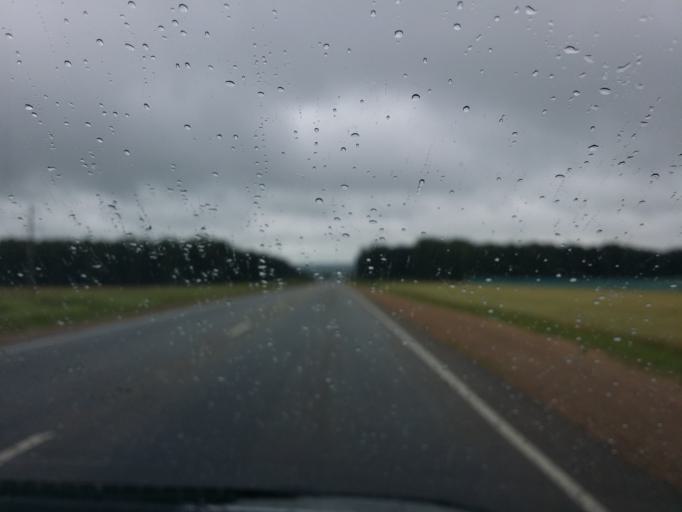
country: RU
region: Altai Krai
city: Nalobikha
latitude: 53.2309
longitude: 84.6037
